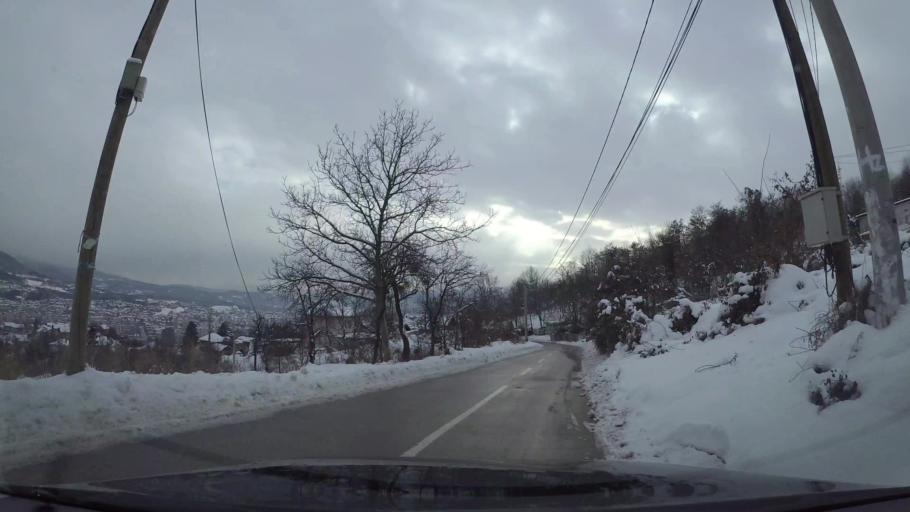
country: BA
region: Federation of Bosnia and Herzegovina
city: Kobilja Glava
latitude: 43.8692
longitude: 18.3883
